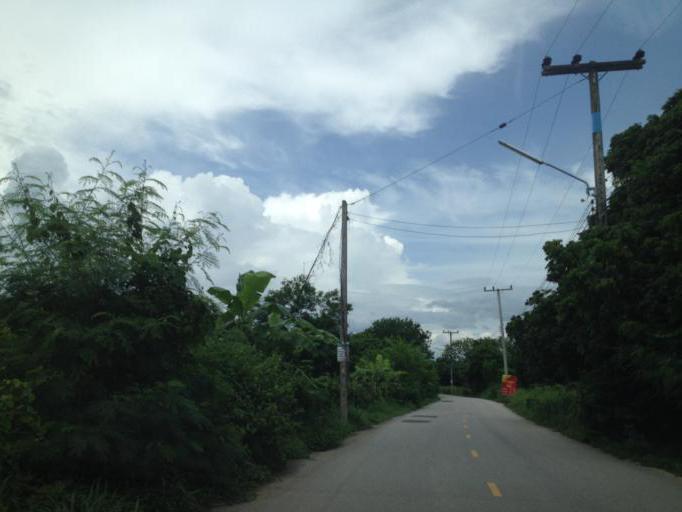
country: TH
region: Chiang Mai
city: Hang Dong
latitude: 18.6862
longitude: 98.8903
